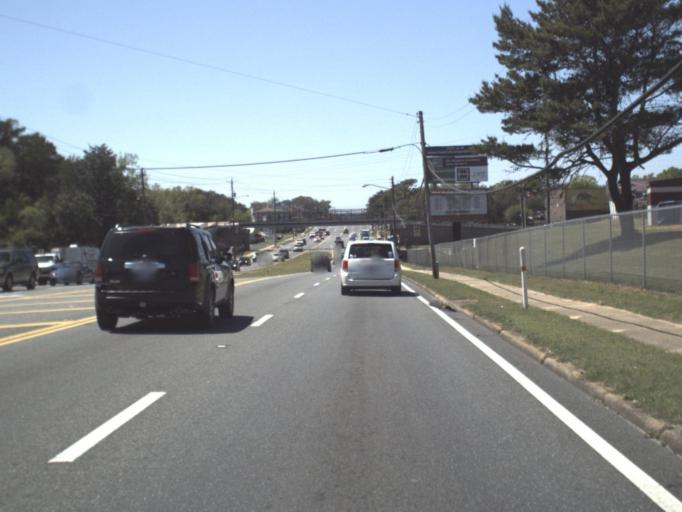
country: US
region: Florida
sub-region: Okaloosa County
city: Niceville
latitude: 30.5179
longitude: -86.4743
